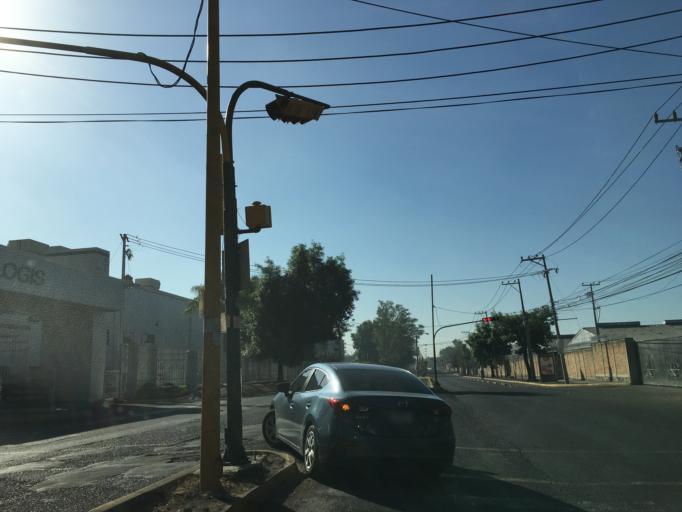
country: MX
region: Jalisco
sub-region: Tlajomulco de Zuniga
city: La Tijera
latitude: 20.6146
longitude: -103.4193
